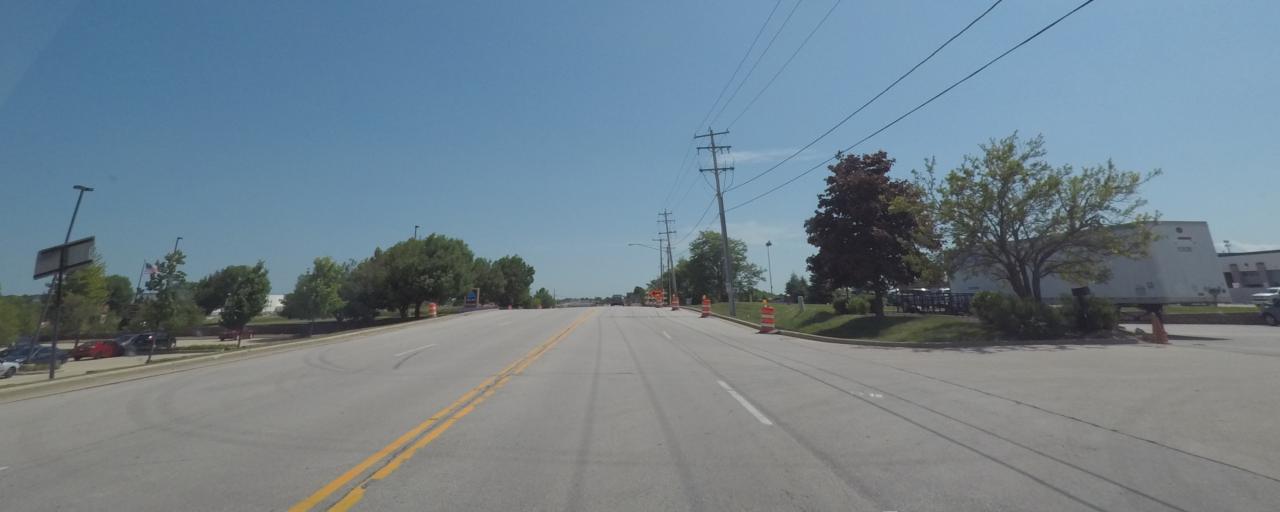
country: US
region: Wisconsin
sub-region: Racine County
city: Caledonia
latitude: 42.8755
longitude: -87.9323
